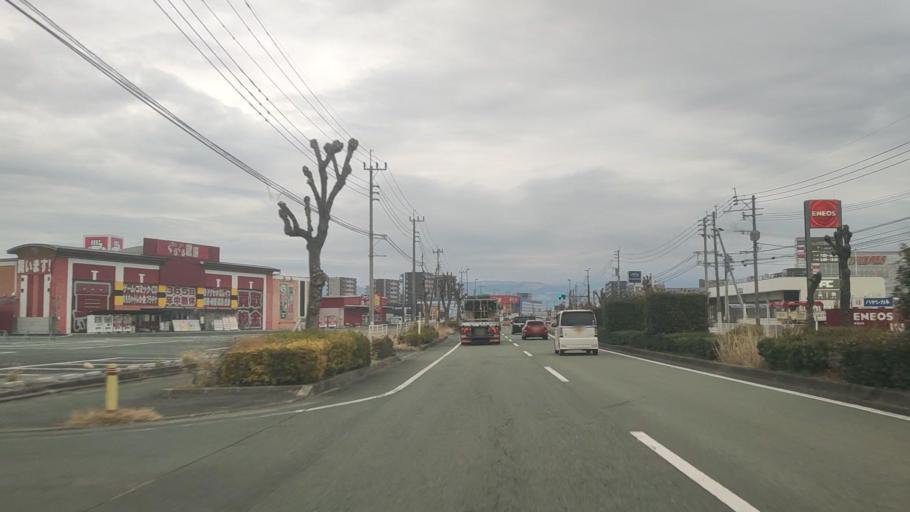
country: JP
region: Kumamoto
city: Ozu
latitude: 32.8616
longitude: 130.8085
